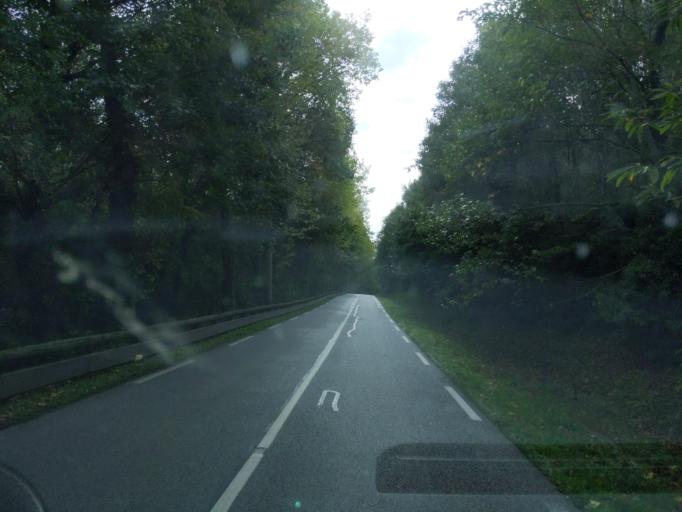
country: FR
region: Ile-de-France
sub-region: Departement des Yvelines
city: Chevreuse
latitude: 48.6931
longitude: 2.0173
